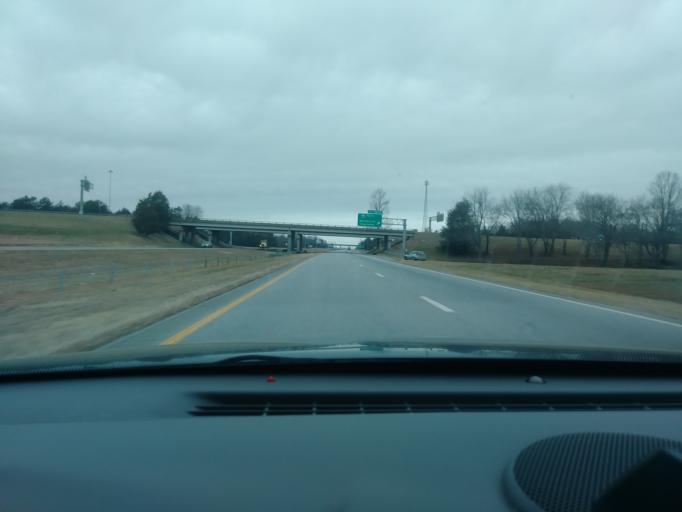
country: US
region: North Carolina
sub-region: Yadkin County
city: Jonesville
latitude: 36.1214
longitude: -80.8121
